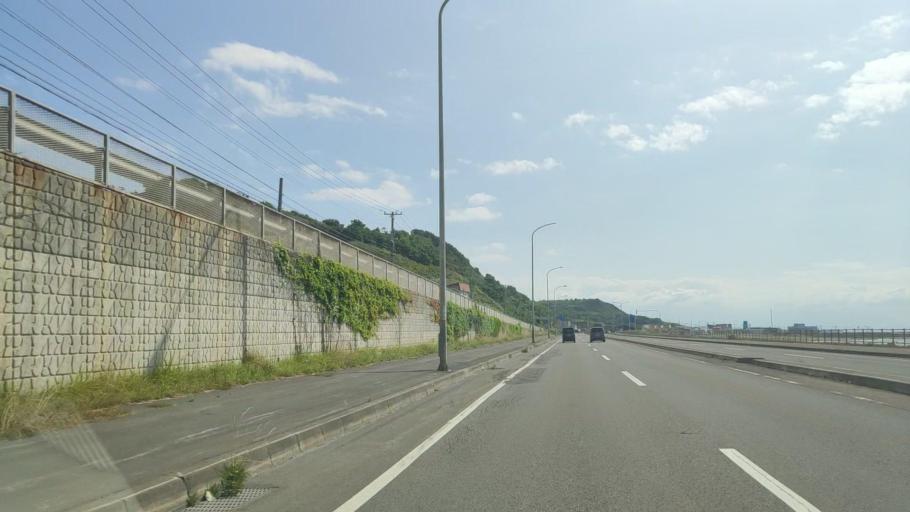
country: JP
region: Hokkaido
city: Rumoi
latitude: 44.0035
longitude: 141.6587
